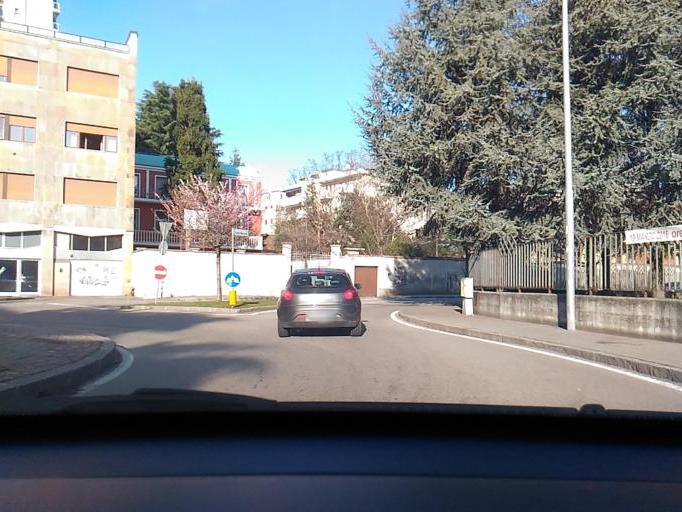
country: IT
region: Lombardy
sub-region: Provincia di Varese
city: Busto Arsizio
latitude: 45.6137
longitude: 8.8467
